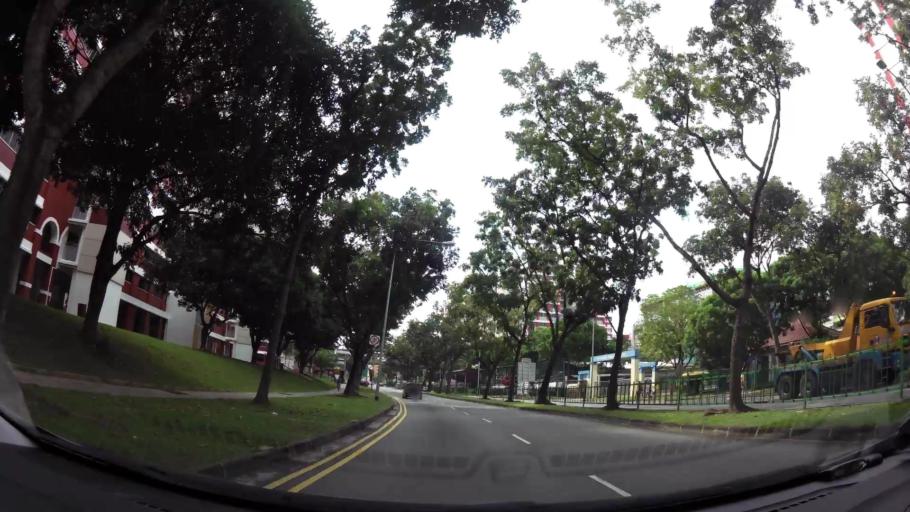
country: MY
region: Johor
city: Kampung Pasir Gudang Baru
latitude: 1.3767
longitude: 103.8953
